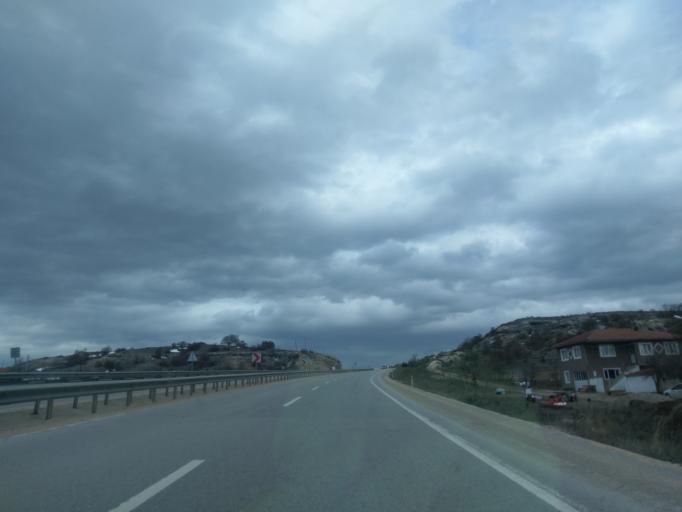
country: TR
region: Eskisehir
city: Eskisehir
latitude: 39.7352
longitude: 30.3848
